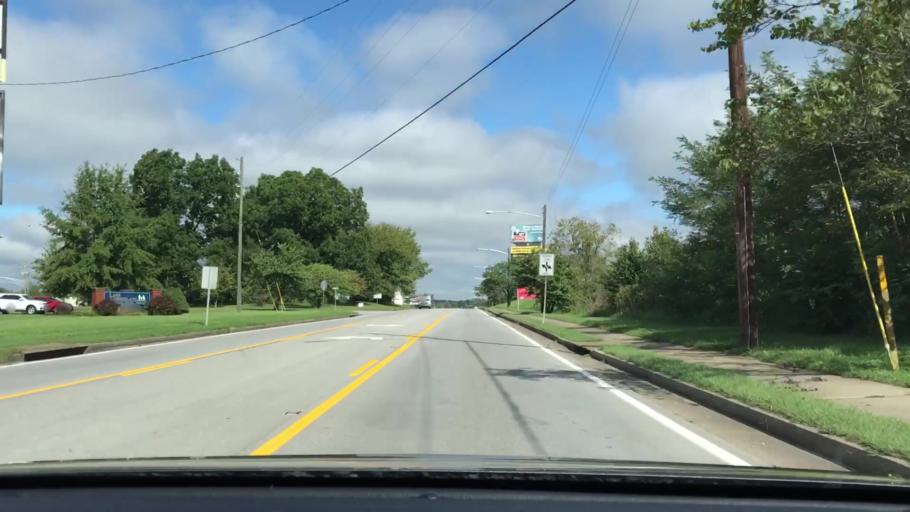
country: US
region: Kentucky
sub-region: Russell County
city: Jamestown
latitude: 37.0036
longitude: -85.0736
